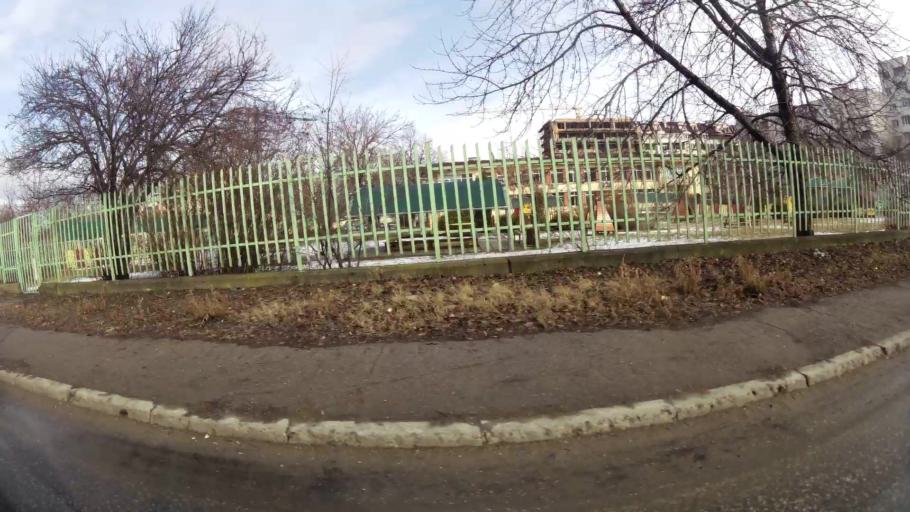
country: BG
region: Sofia-Capital
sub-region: Stolichna Obshtina
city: Sofia
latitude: 42.7174
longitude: 23.2741
